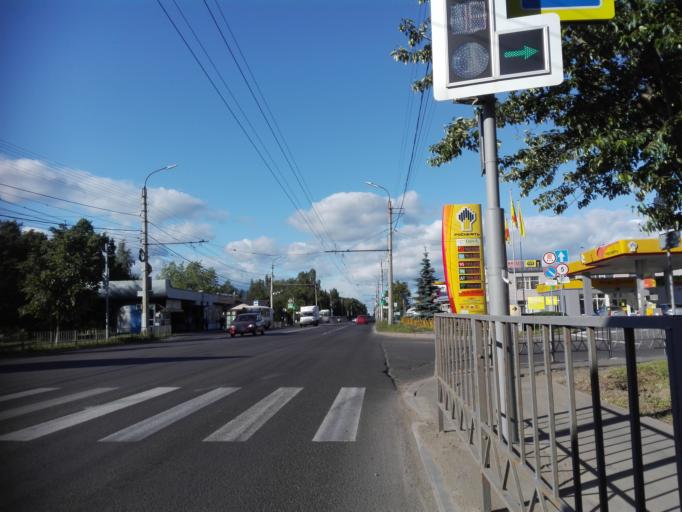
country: RU
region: Orjol
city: Orel
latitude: 53.0007
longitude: 36.1389
